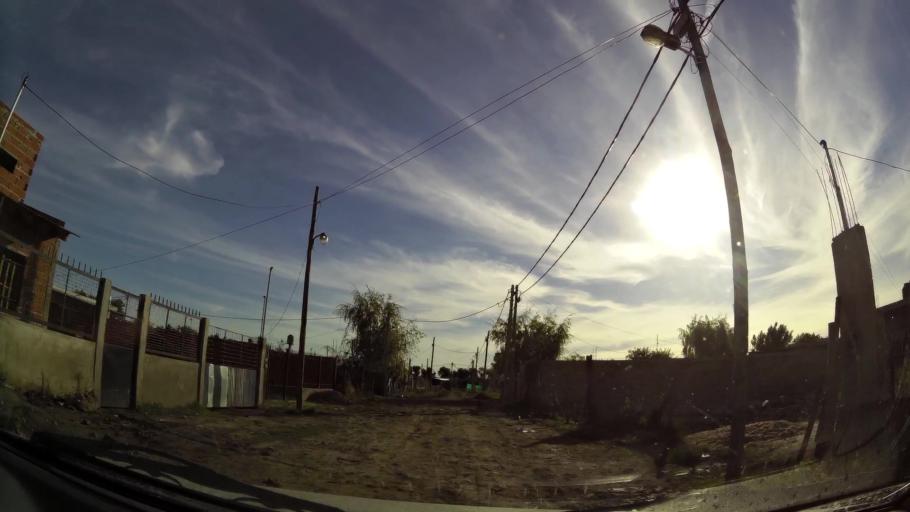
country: AR
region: Buenos Aires
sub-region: Partido de Almirante Brown
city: Adrogue
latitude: -34.8196
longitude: -58.3233
